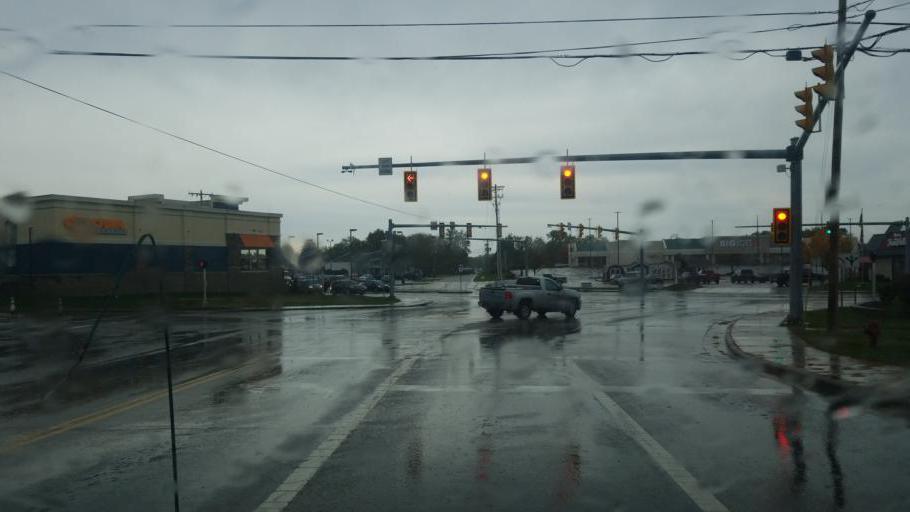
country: US
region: Ohio
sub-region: Washington County
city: Marietta
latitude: 39.4156
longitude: -81.4445
